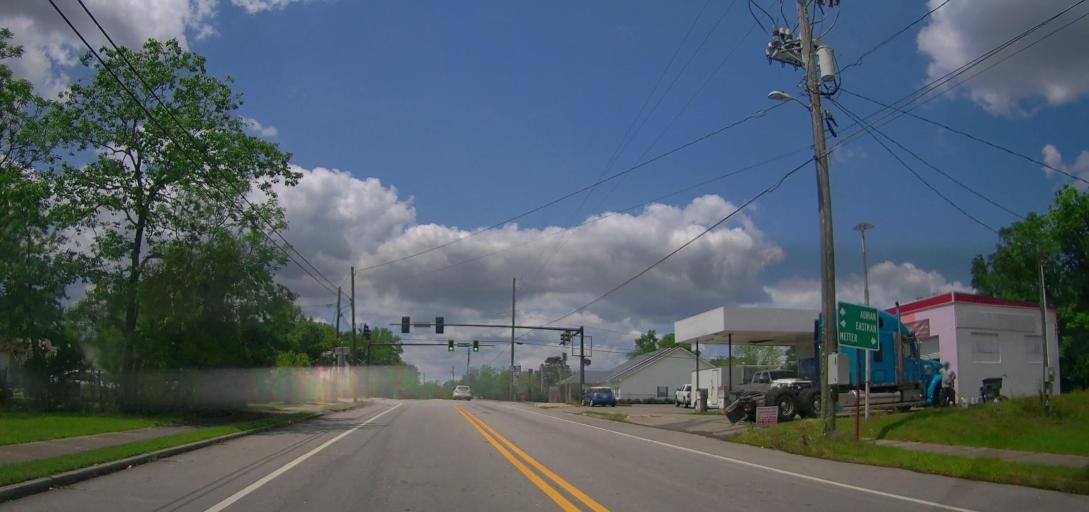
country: US
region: Georgia
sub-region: Treutlen County
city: Soperton
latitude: 32.3797
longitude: -82.5924
